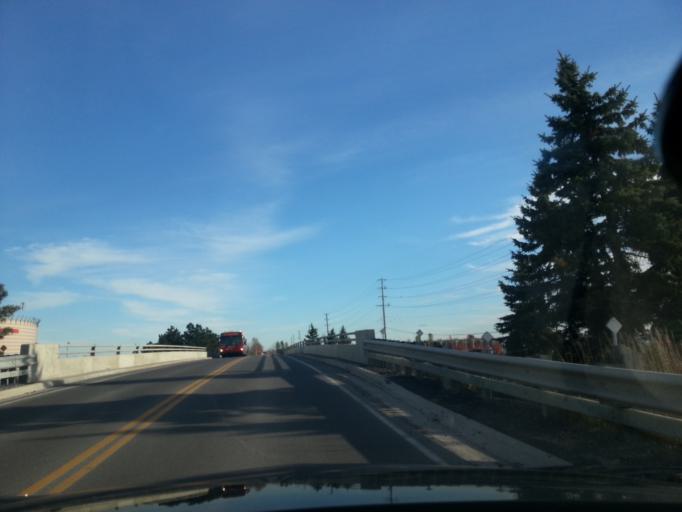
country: CA
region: Ontario
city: Bells Corners
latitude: 45.2979
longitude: -75.9318
